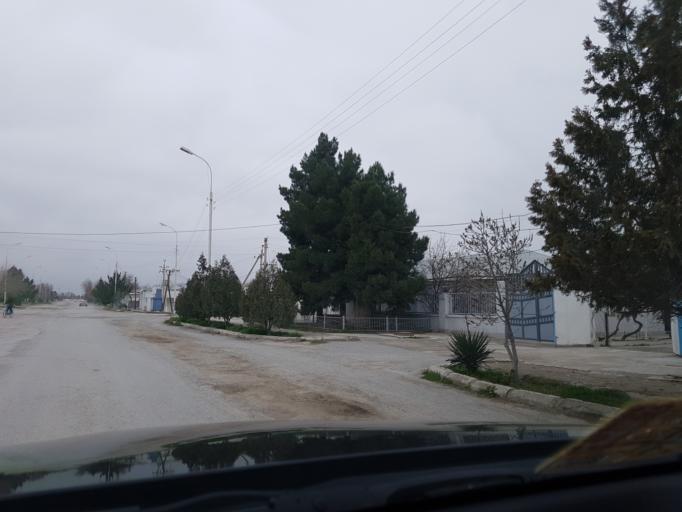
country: TM
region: Ahal
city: Abadan
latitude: 38.1591
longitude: 57.9571
